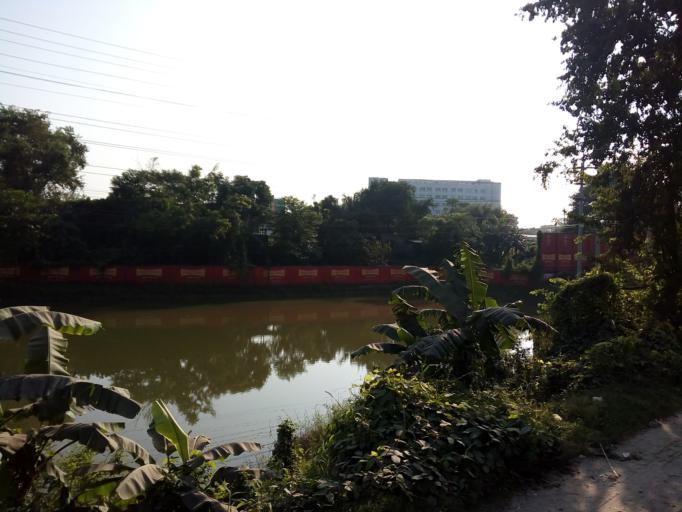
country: BD
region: Dhaka
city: Tungi
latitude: 23.9171
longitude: 90.2392
